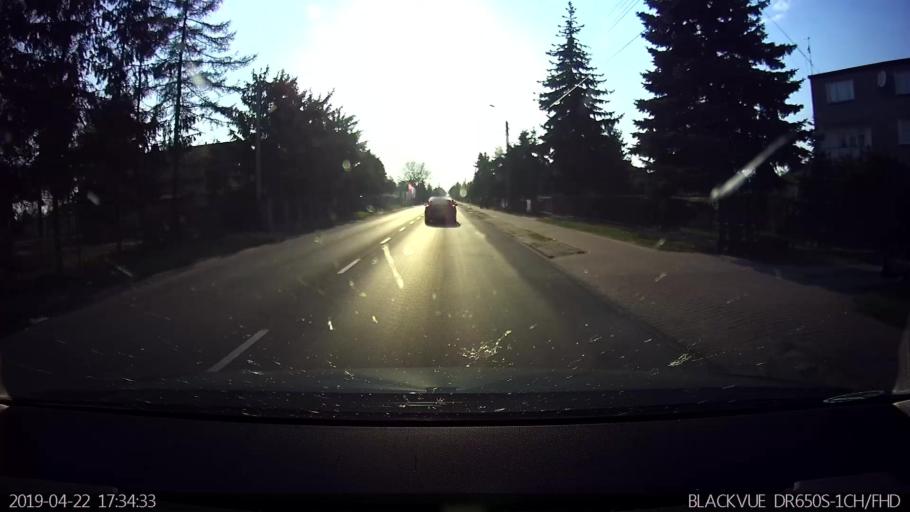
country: PL
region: Masovian Voivodeship
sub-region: Powiat sokolowski
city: Sokolow Podlaski
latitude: 52.4073
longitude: 22.2140
